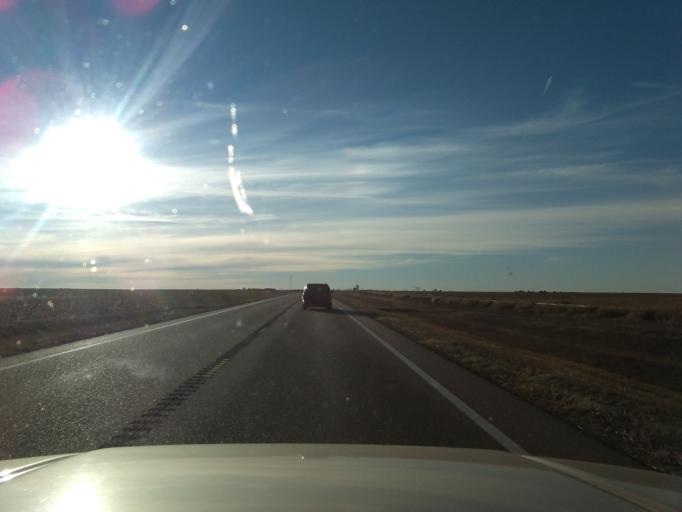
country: US
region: Kansas
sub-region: Thomas County
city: Colby
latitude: 39.4622
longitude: -100.7706
